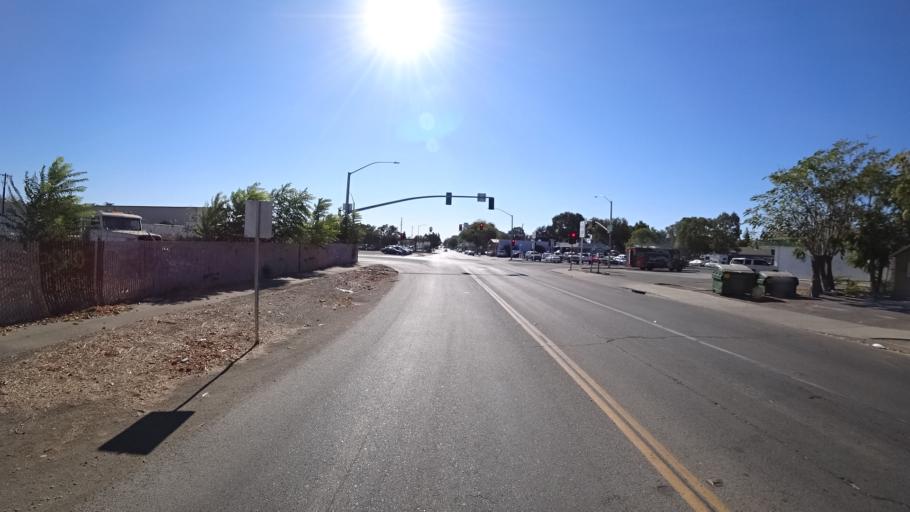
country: US
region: California
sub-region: Yolo County
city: Winters
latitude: 38.5255
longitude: -121.9709
